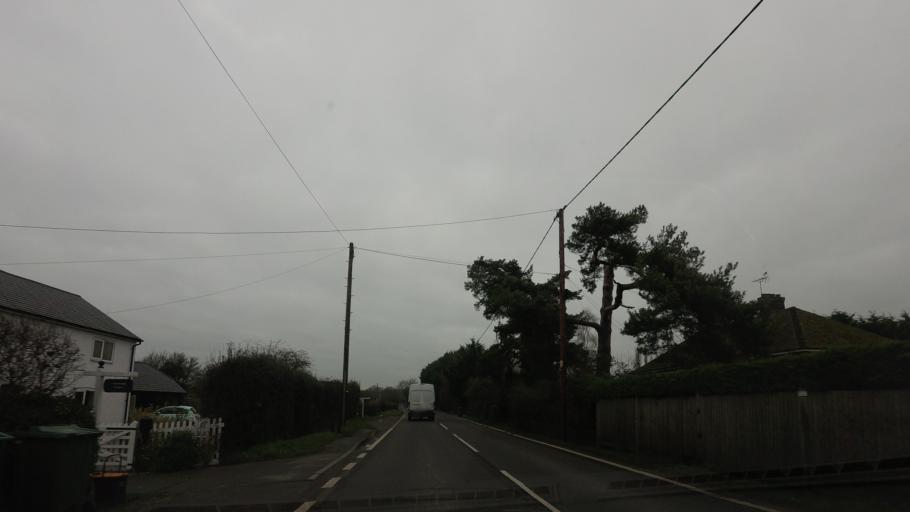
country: GB
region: England
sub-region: Kent
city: Staplehurst
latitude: 51.1378
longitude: 0.5552
